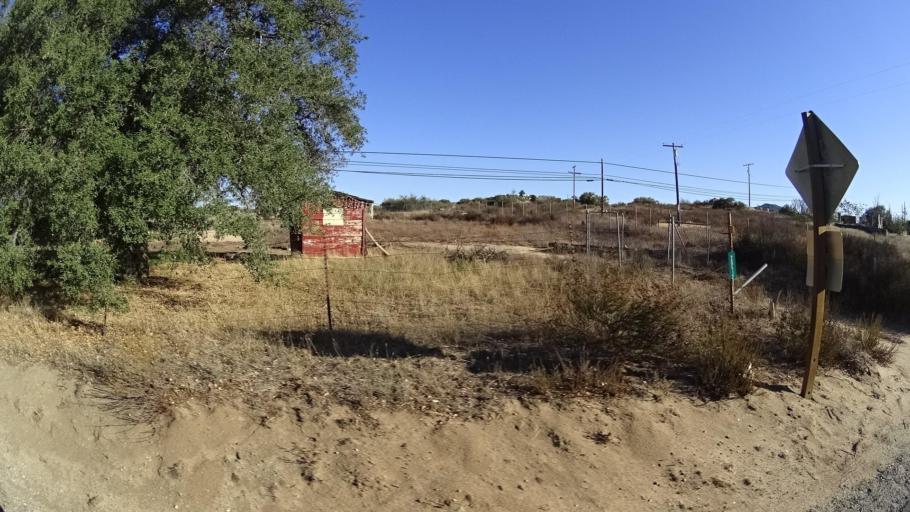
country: MX
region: Baja California
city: Tecate
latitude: 32.5998
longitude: -116.5834
